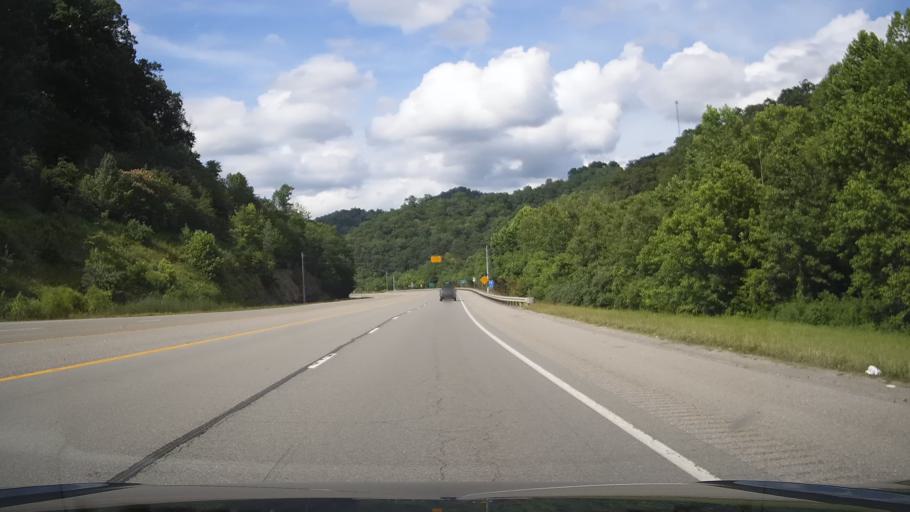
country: US
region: Kentucky
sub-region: Floyd County
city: Prestonsburg
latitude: 37.7197
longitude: -82.7900
